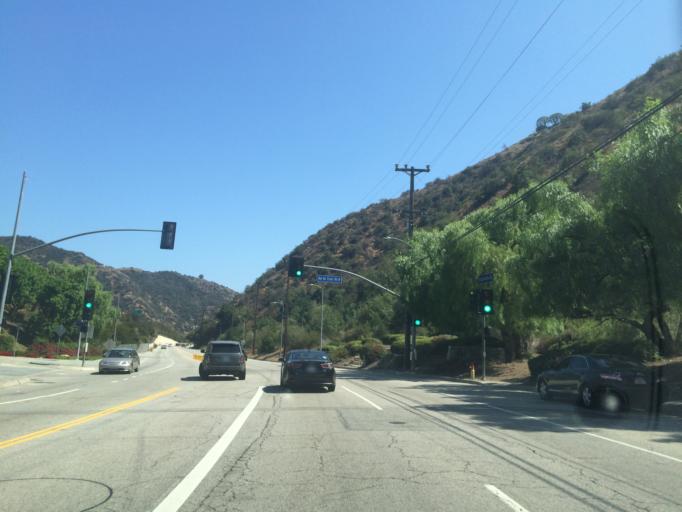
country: US
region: California
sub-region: Los Angeles County
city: Sherman Oaks
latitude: 34.1106
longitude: -118.4827
